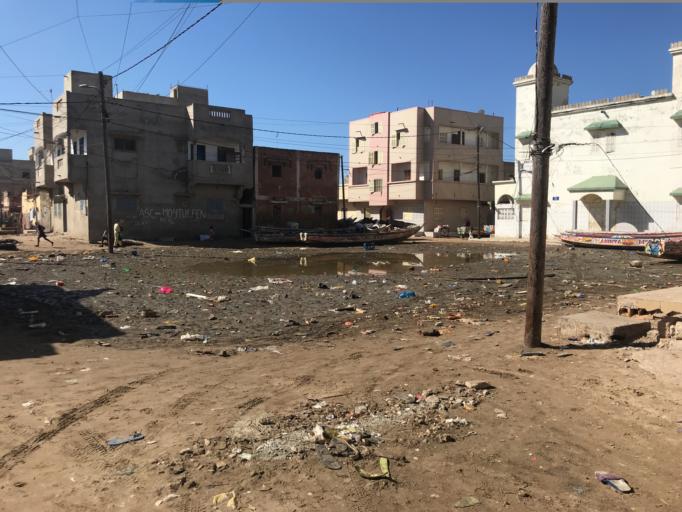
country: SN
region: Saint-Louis
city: Saint-Louis
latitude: 16.0327
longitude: -16.5081
